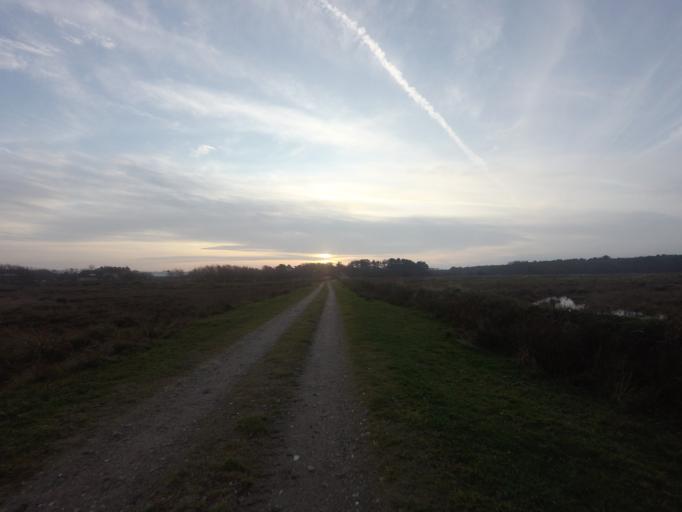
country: NL
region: North Holland
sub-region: Gemeente Texel
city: Den Burg
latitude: 53.1056
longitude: 4.7746
